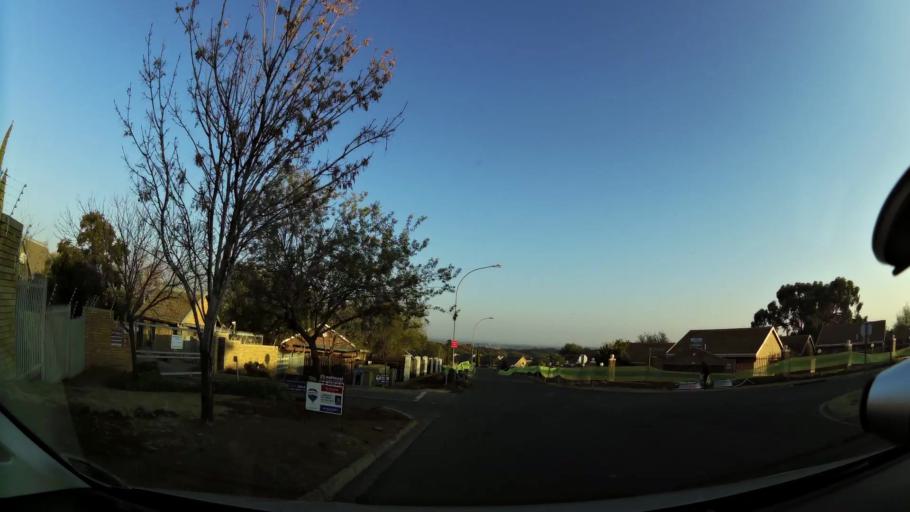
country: ZA
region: Orange Free State
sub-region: Mangaung Metropolitan Municipality
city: Bloemfontein
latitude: -29.0887
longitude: 26.1629
